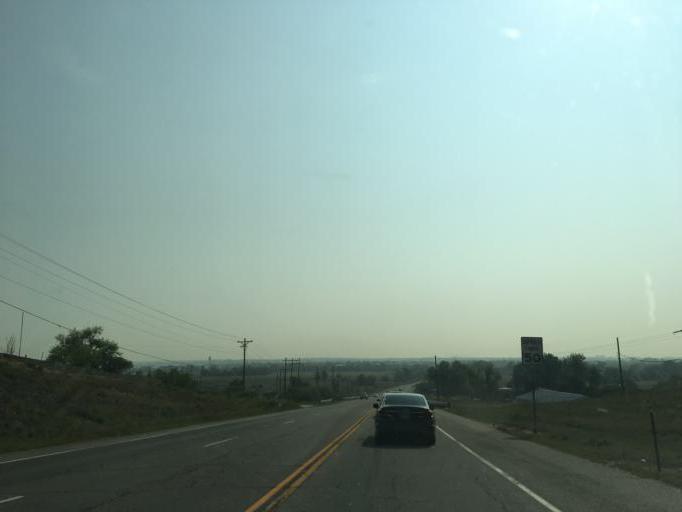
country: US
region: Colorado
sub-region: Adams County
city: Todd Creek
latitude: 39.9870
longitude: -104.8492
